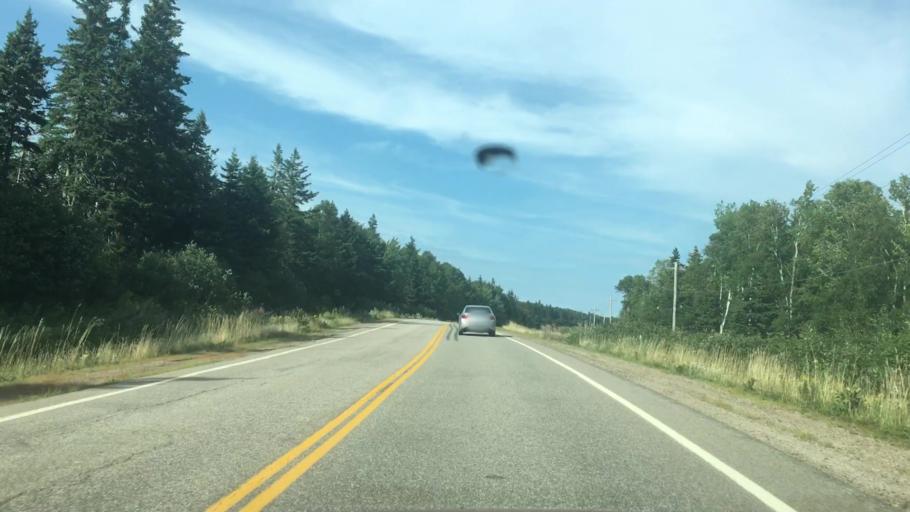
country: CA
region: Nova Scotia
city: Sydney Mines
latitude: 46.7156
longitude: -60.3526
